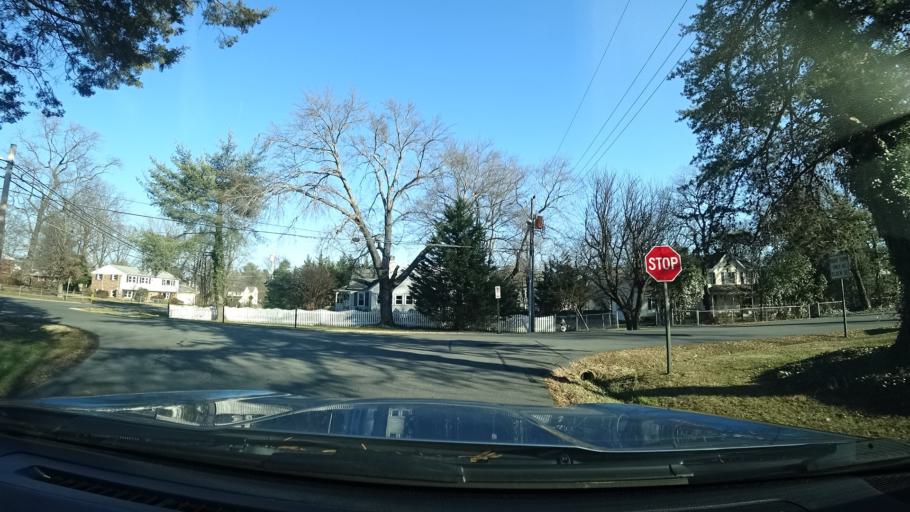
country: US
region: Virginia
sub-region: Fairfax County
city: Herndon
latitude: 38.9716
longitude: -77.3793
